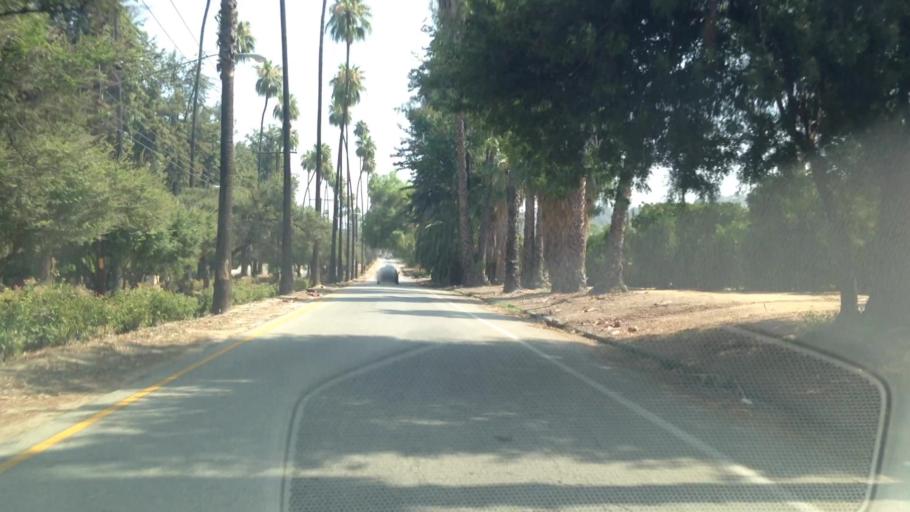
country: US
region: California
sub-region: Riverside County
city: Riverside
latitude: 33.9406
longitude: -117.3733
